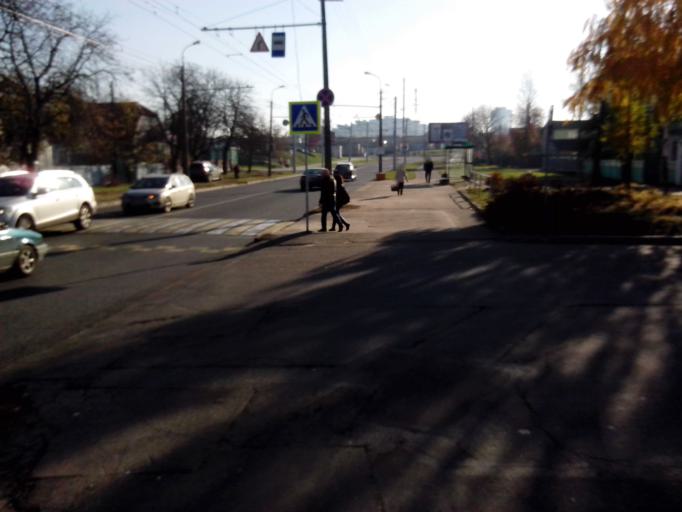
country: BY
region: Minsk
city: Minsk
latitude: 53.9507
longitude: 27.5965
